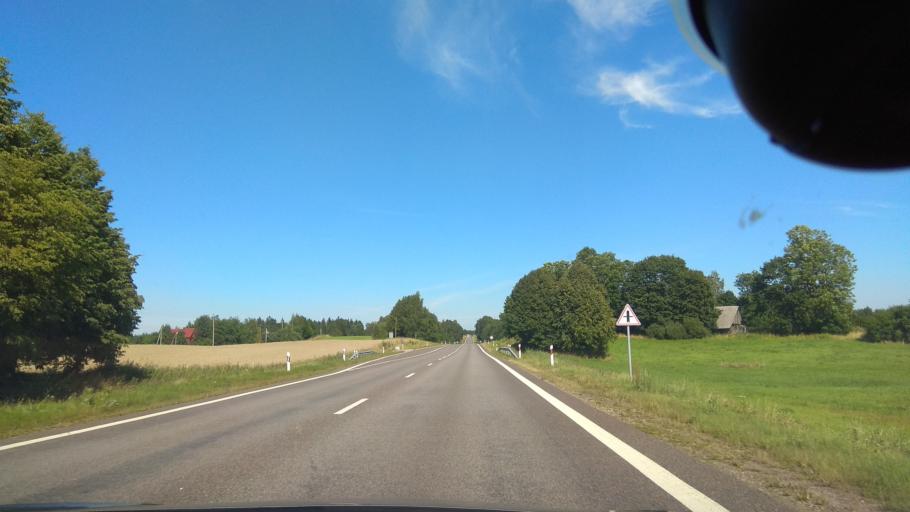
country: LT
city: Seda
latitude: 55.9877
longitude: 22.0437
